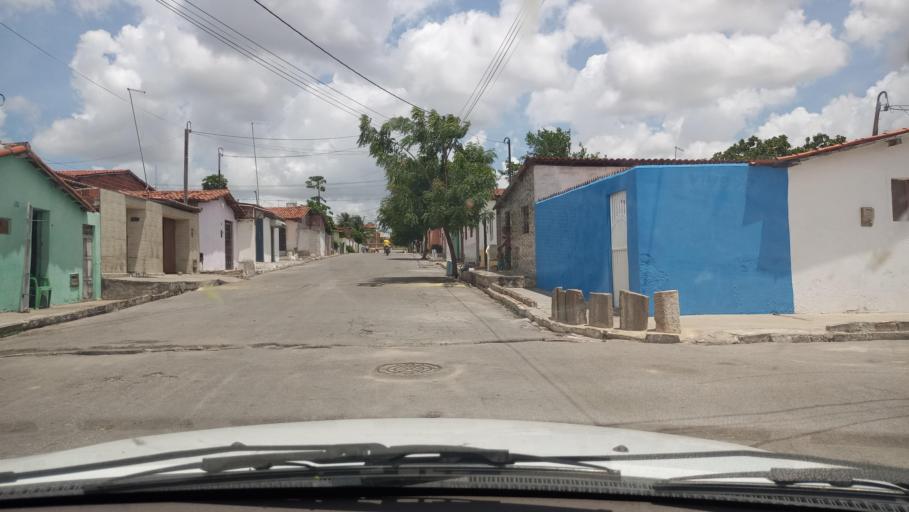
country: BR
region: Rio Grande do Norte
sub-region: Tangara
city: Tangara
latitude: -6.1009
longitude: -35.7100
